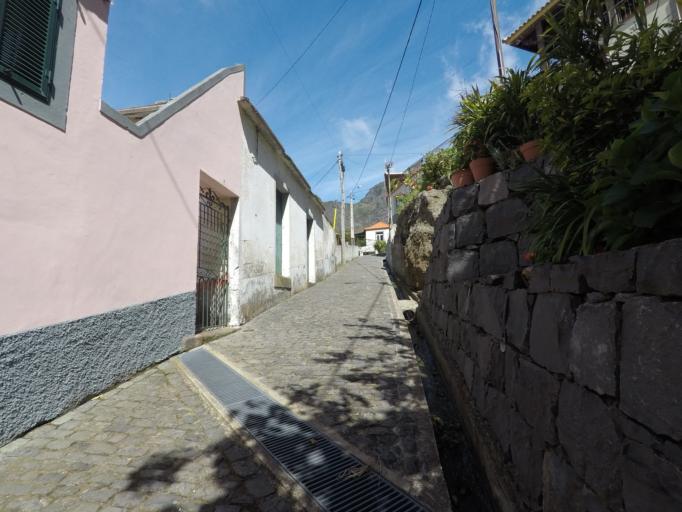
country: PT
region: Madeira
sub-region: Camara de Lobos
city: Curral das Freiras
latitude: 32.7208
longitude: -16.9654
